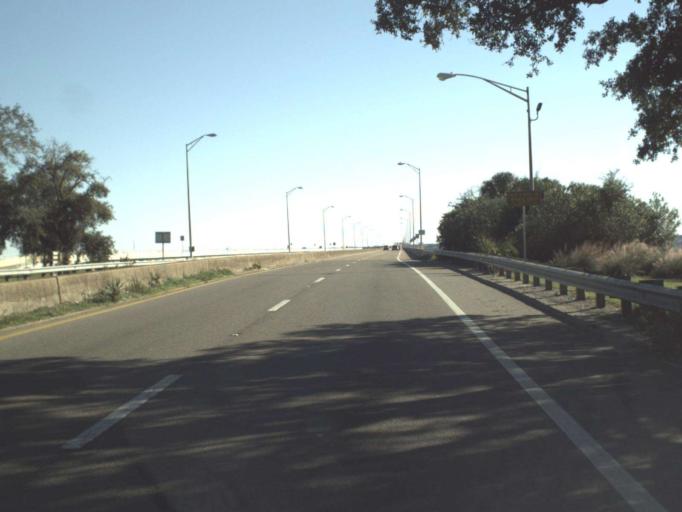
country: US
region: Florida
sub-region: Escambia County
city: East Pensacola Heights
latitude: 30.4154
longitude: -87.1929
